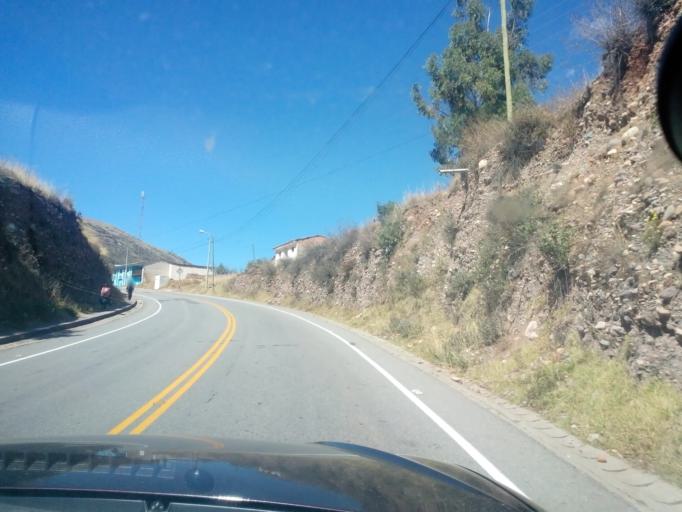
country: PE
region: Cusco
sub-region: Provincia de Canchis
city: Checacupe
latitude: -14.0270
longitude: -71.4565
